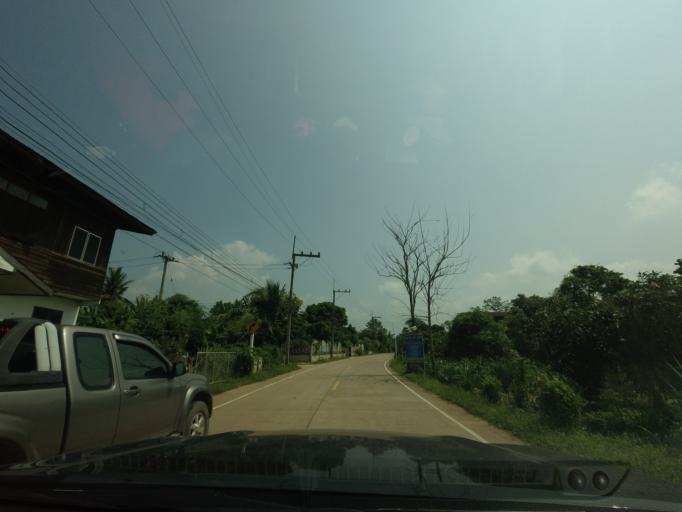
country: TH
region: Nan
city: Nan
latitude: 18.8611
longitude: 100.8134
